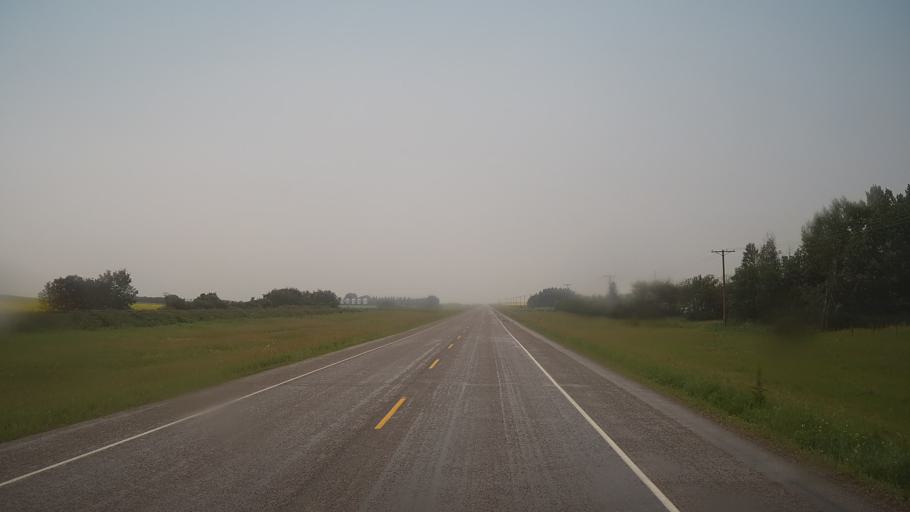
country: CA
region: Saskatchewan
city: Biggar
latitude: 52.1349
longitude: -108.1649
